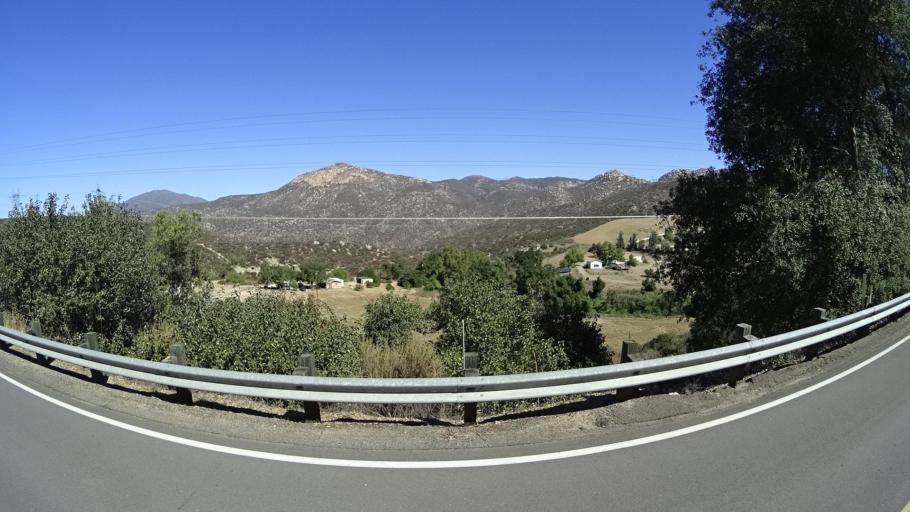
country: US
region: California
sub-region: San Diego County
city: Alpine
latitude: 32.7760
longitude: -116.7112
